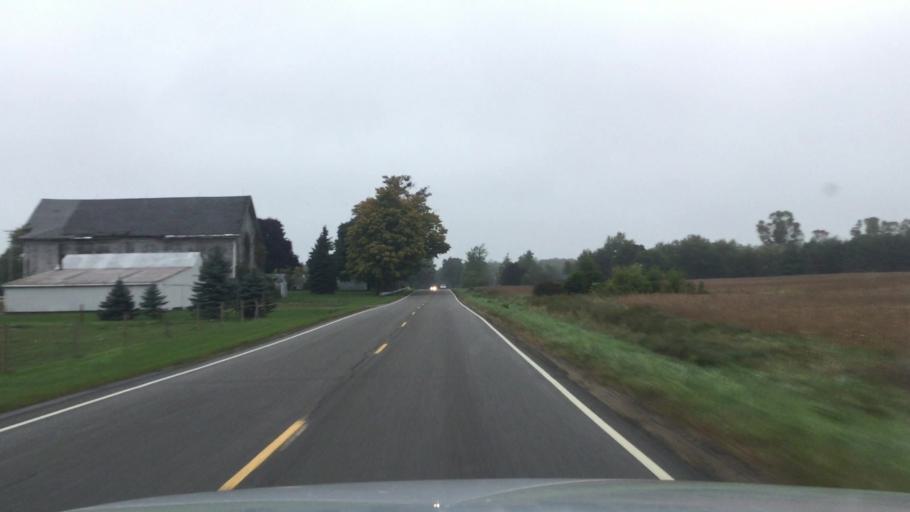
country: US
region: Michigan
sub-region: Shiawassee County
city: Corunna
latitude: 42.9247
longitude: -84.1242
